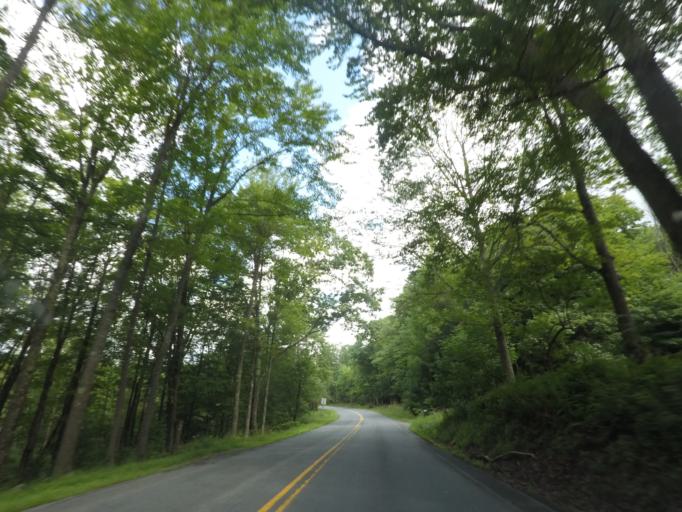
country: US
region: New York
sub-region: Rensselaer County
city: Averill Park
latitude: 42.6488
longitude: -73.4957
